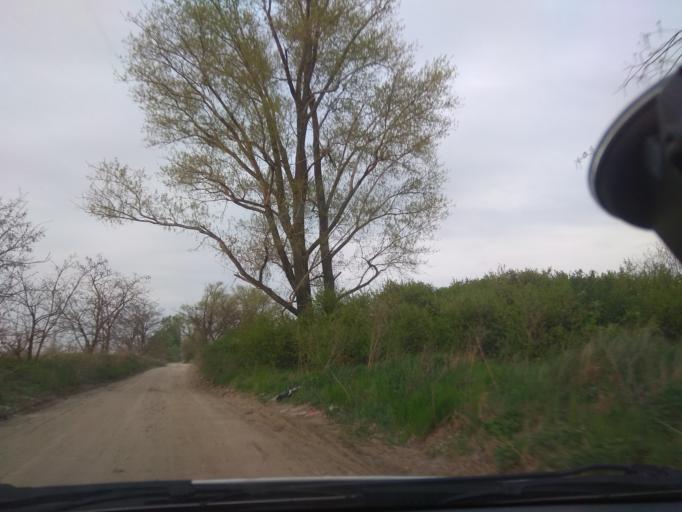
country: HU
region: Pest
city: Szigethalom
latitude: 47.3420
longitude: 19.0051
